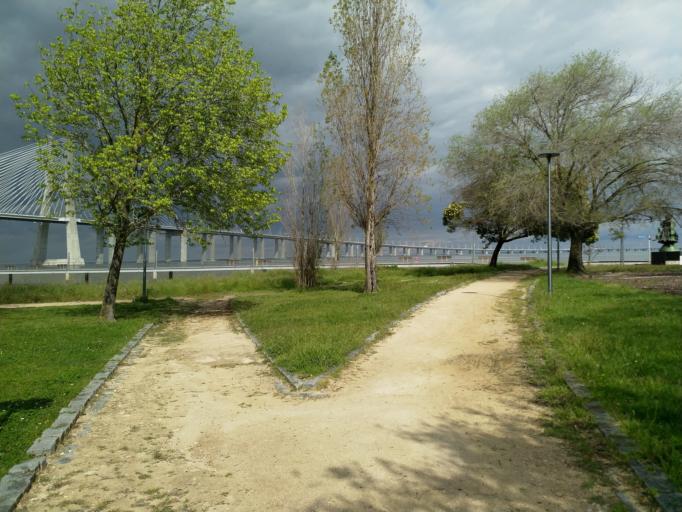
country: PT
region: Lisbon
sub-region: Loures
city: Moscavide
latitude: 38.7816
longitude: -9.0919
